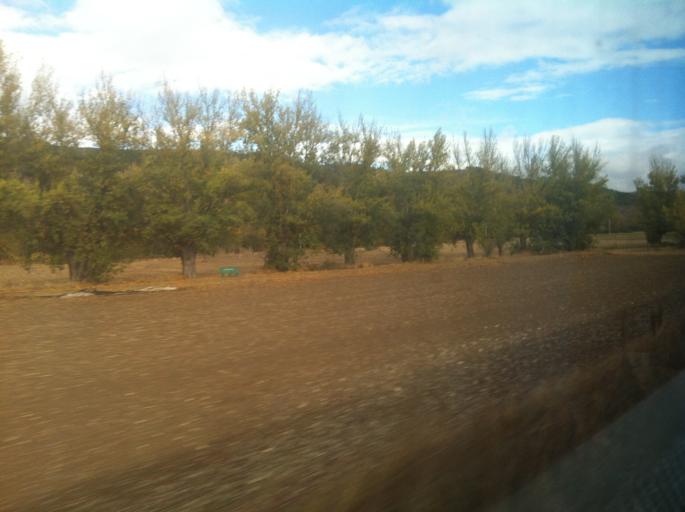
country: ES
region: Castille and Leon
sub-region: Provincia de Burgos
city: Pradanos de Bureba
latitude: 42.5076
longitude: -3.3433
